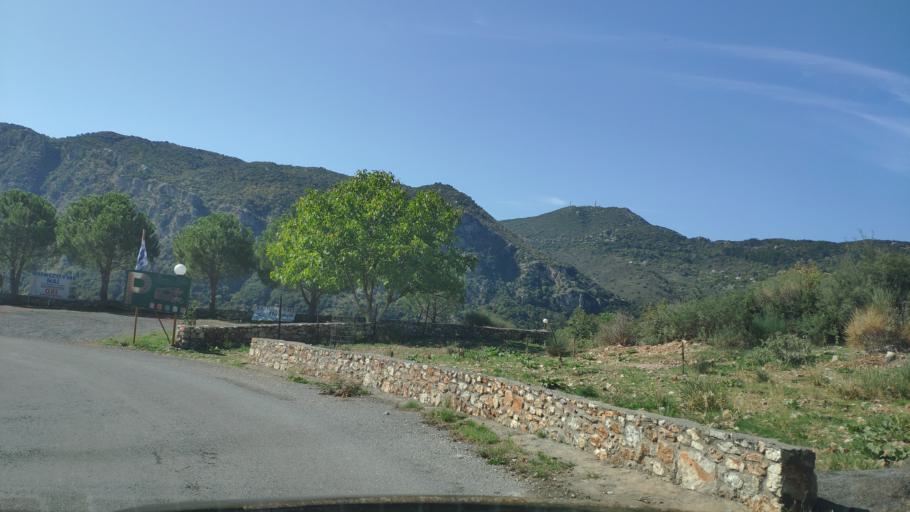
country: GR
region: Peloponnese
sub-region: Nomos Arkadias
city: Dimitsana
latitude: 37.5869
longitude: 22.0447
